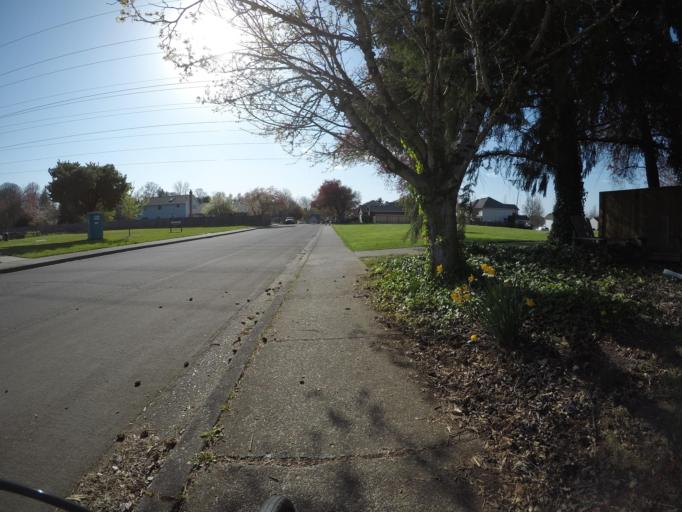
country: US
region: Oregon
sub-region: Washington County
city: Oak Hills
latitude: 45.5484
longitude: -122.8465
